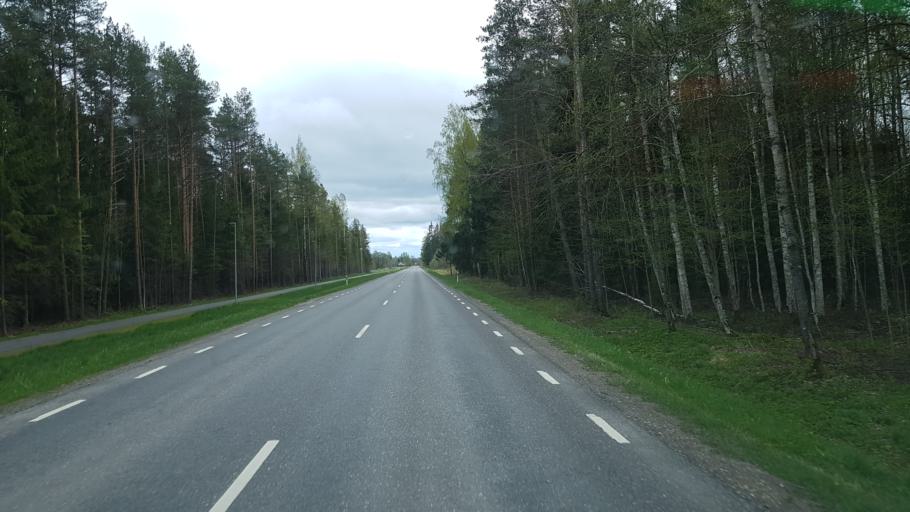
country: EE
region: Paernumaa
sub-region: Tootsi vald
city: Tootsi
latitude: 58.4982
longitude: 24.8021
